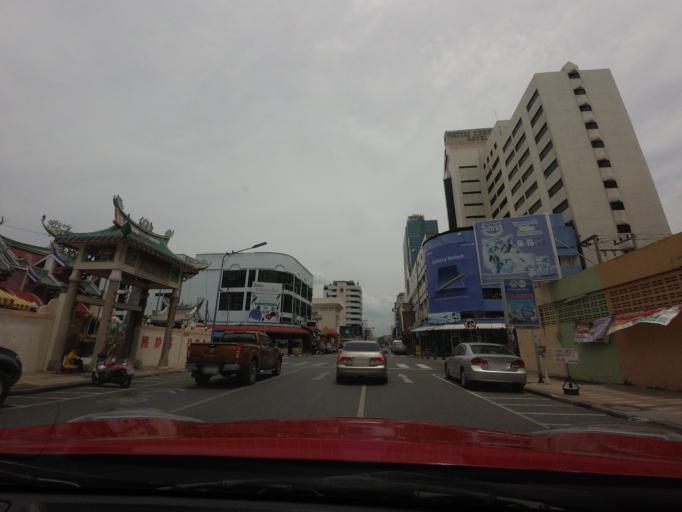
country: TH
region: Songkhla
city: Hat Yai
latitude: 7.0022
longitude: 100.4711
